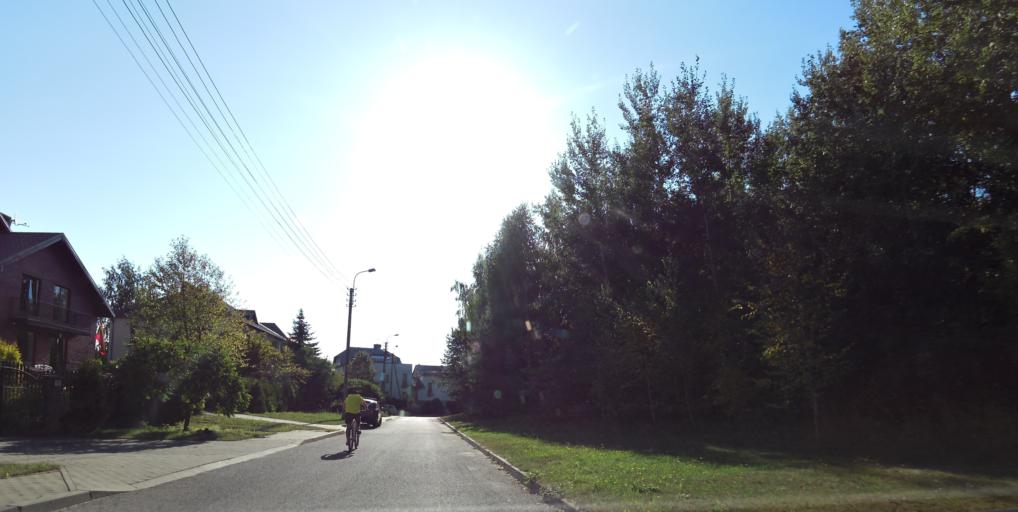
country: LT
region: Vilnius County
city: Pilaite
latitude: 54.7130
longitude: 25.1908
